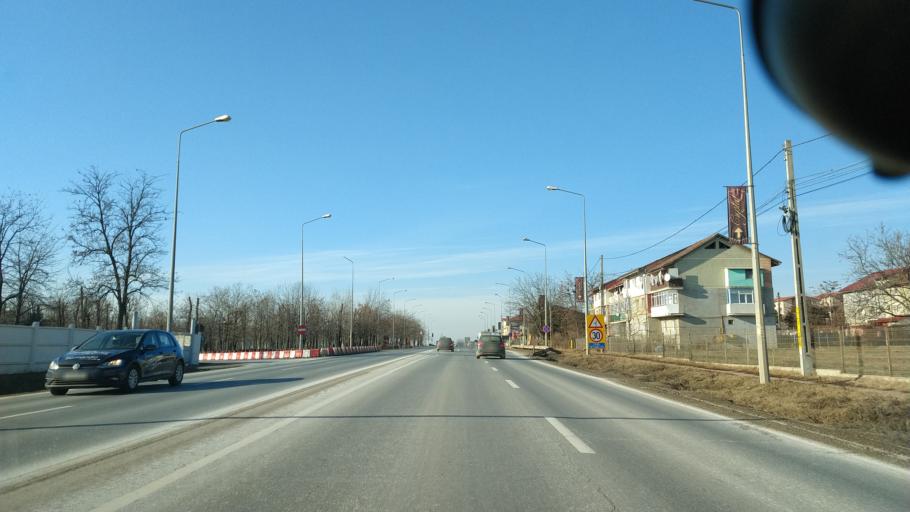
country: RO
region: Iasi
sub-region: Comuna Valea Lupului
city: Valea Lupului
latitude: 47.1766
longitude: 27.4926
